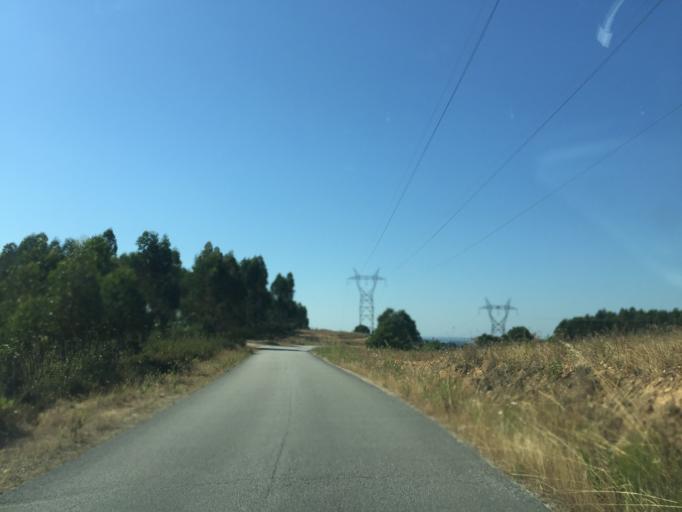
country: PT
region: Santarem
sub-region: Tomar
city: Tomar
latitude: 39.5658
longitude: -8.3208
